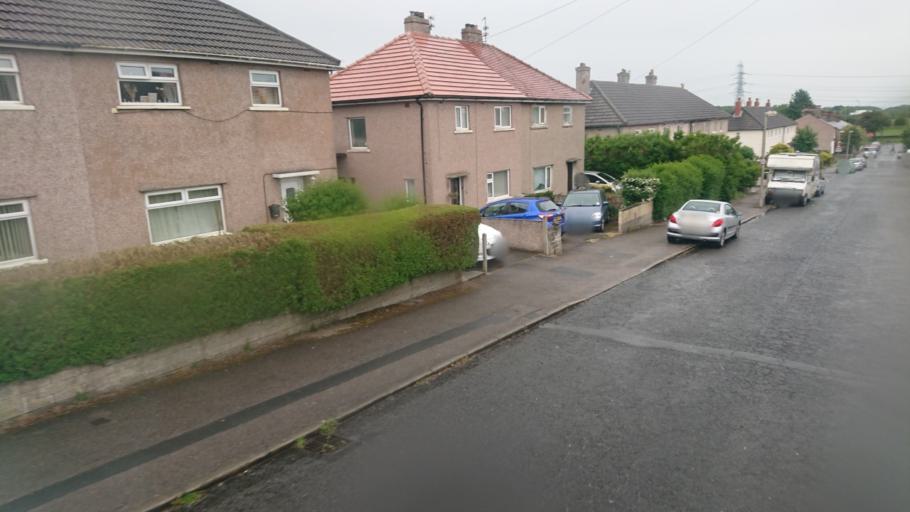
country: GB
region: England
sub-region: Lancashire
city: Morecambe
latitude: 54.0376
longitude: -2.8977
